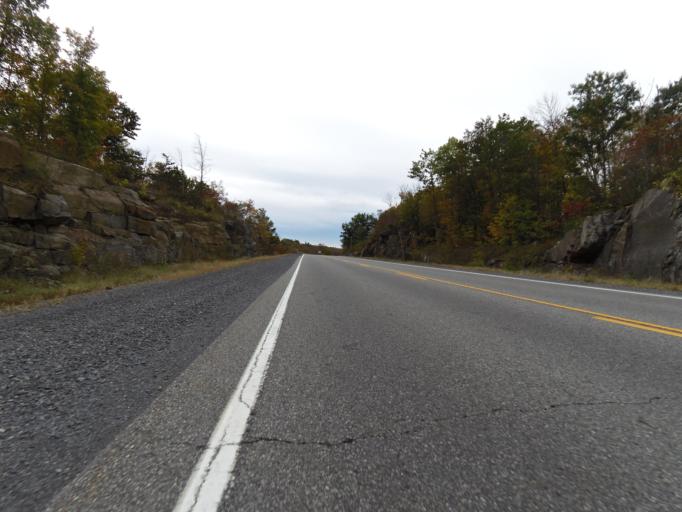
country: CA
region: Ontario
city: Gananoque
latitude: 44.4011
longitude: -76.3133
